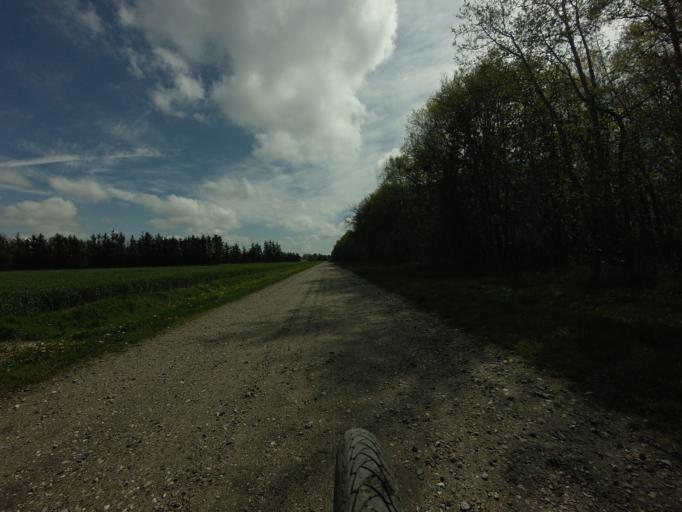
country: DK
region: North Denmark
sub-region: Jammerbugt Kommune
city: Kas
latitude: 57.1993
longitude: 9.6139
